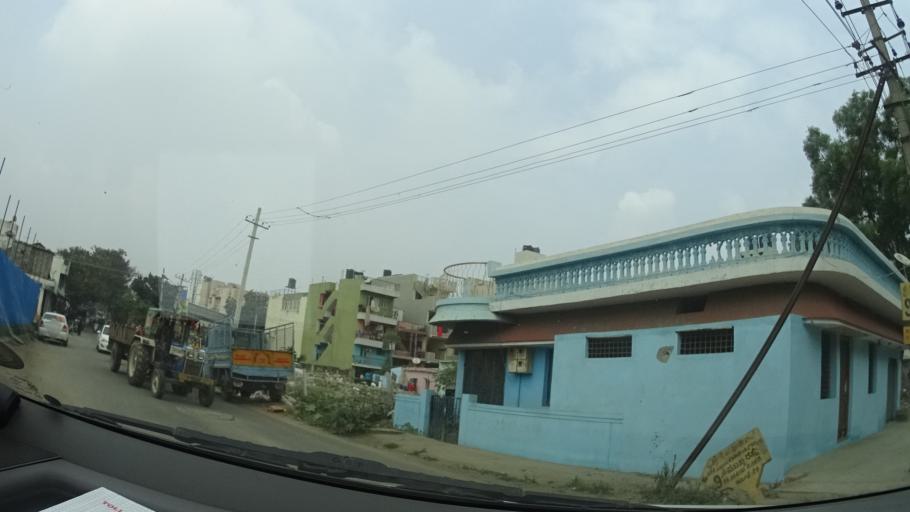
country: IN
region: Karnataka
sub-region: Bangalore Urban
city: Bangalore
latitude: 13.0342
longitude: 77.6245
